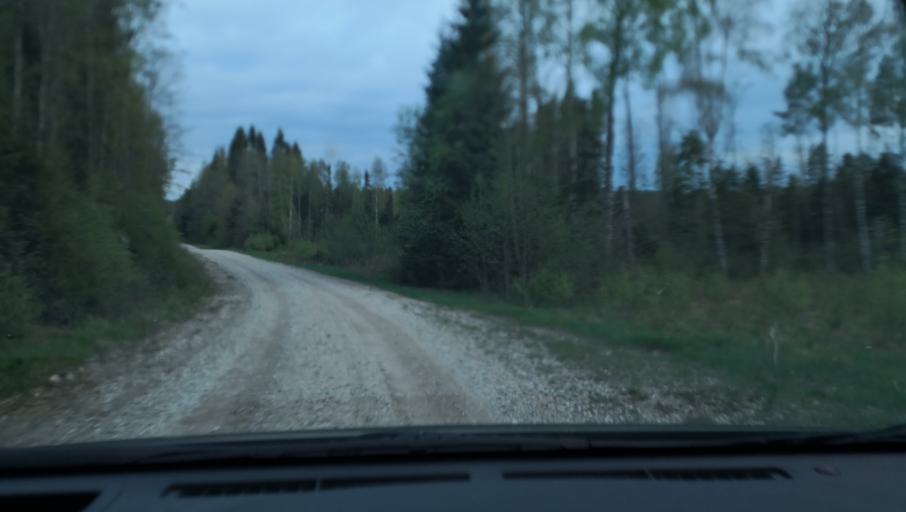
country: SE
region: Vaestmanland
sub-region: Skinnskattebergs Kommun
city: Skinnskatteberg
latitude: 59.7722
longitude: 15.4539
